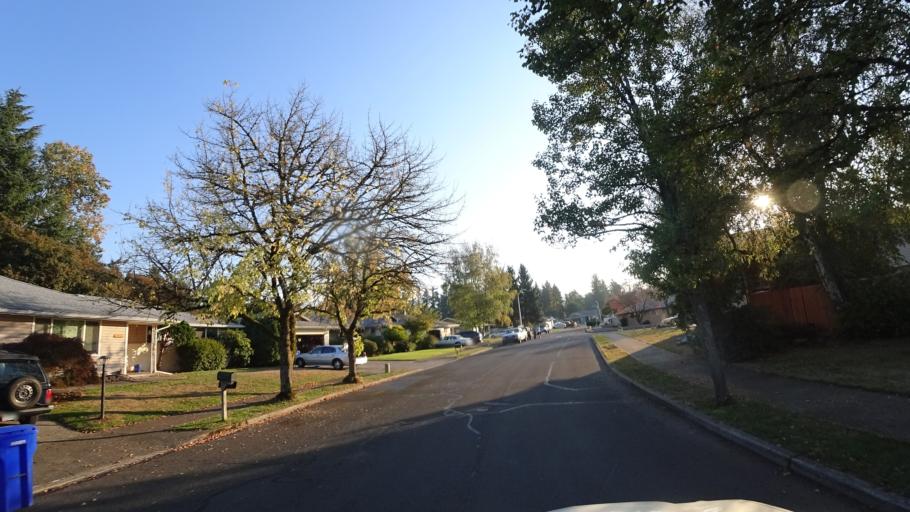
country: US
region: Oregon
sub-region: Multnomah County
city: Gresham
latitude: 45.5140
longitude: -122.4427
